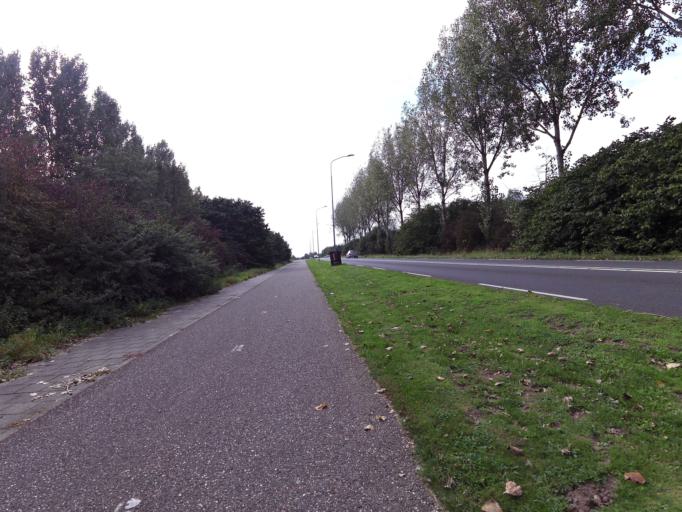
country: NL
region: Gelderland
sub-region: Gemeente Duiven
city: Duiven
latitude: 51.9510
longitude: 5.9999
